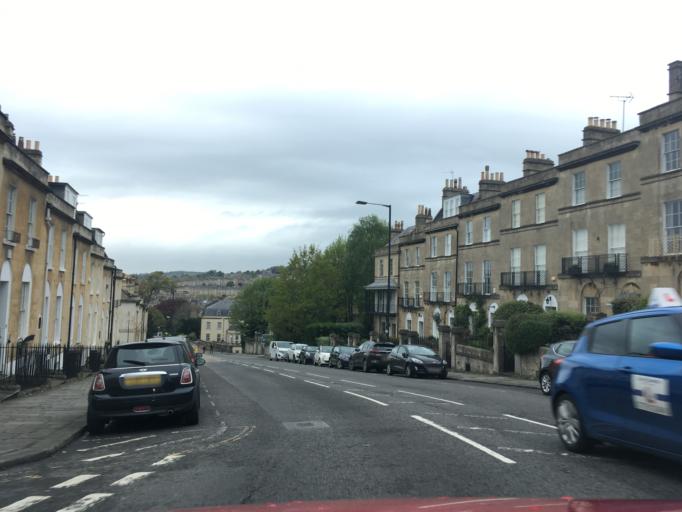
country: GB
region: England
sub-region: Bath and North East Somerset
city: Bath
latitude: 51.3823
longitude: -2.3473
